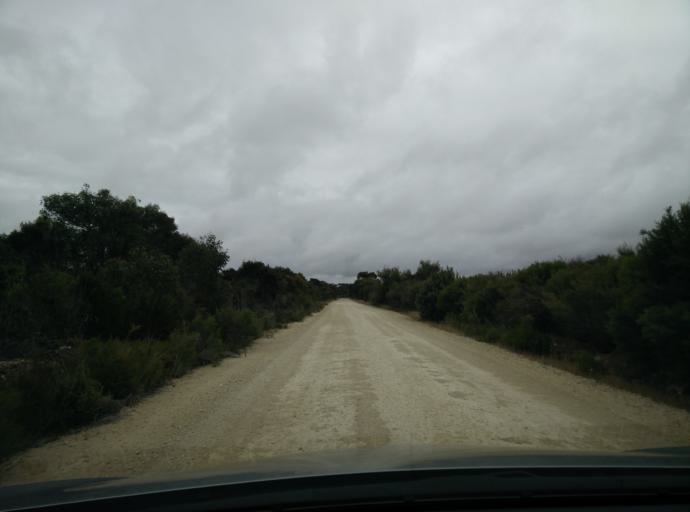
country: AU
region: South Australia
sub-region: Kangaroo Island
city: Kingscote
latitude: -35.8734
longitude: 137.4927
